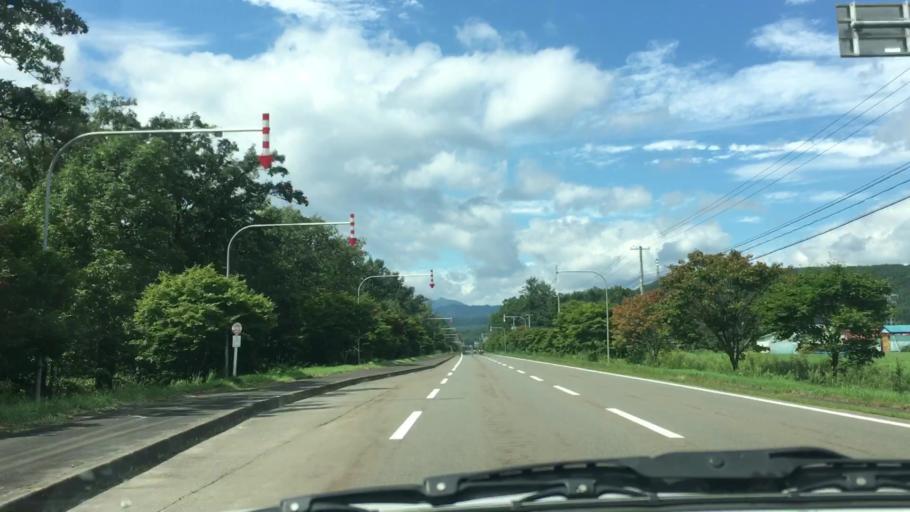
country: JP
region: Hokkaido
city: Otofuke
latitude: 43.3151
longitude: 143.3055
